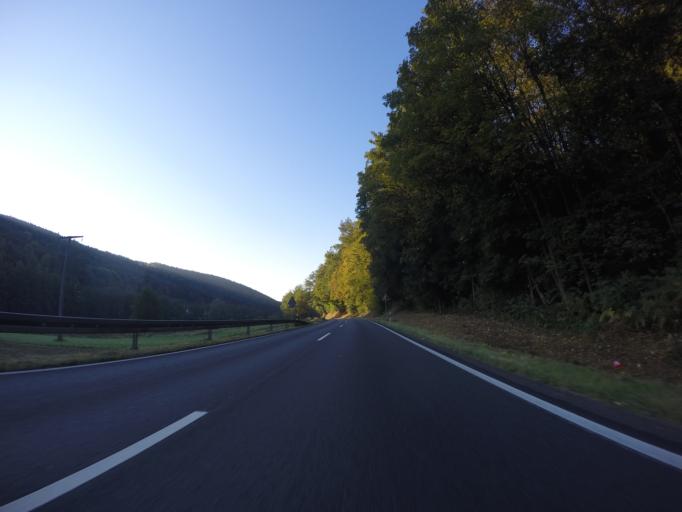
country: DE
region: Bavaria
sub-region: Regierungsbezirk Unterfranken
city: Hasloch
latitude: 49.8048
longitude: 9.4959
